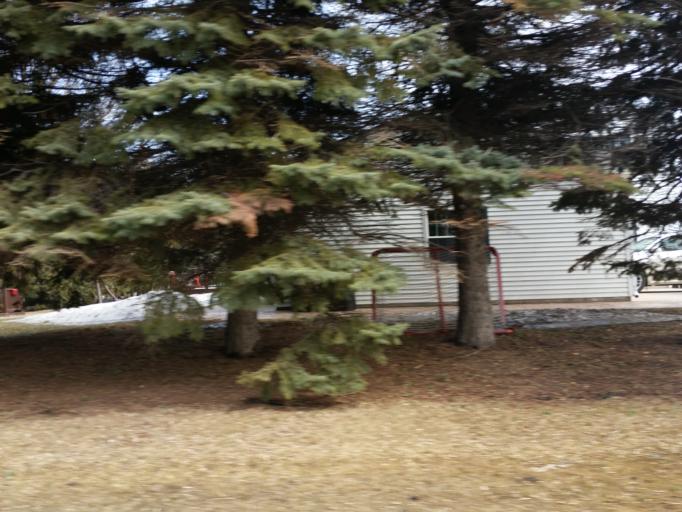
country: US
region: North Dakota
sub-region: Walsh County
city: Grafton
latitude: 48.4084
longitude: -97.4220
